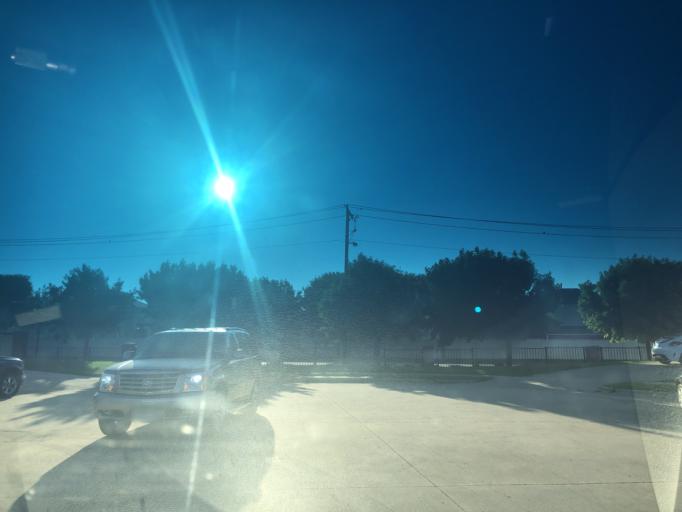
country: US
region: Texas
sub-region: Dallas County
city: Grand Prairie
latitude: 32.7004
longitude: -97.0188
